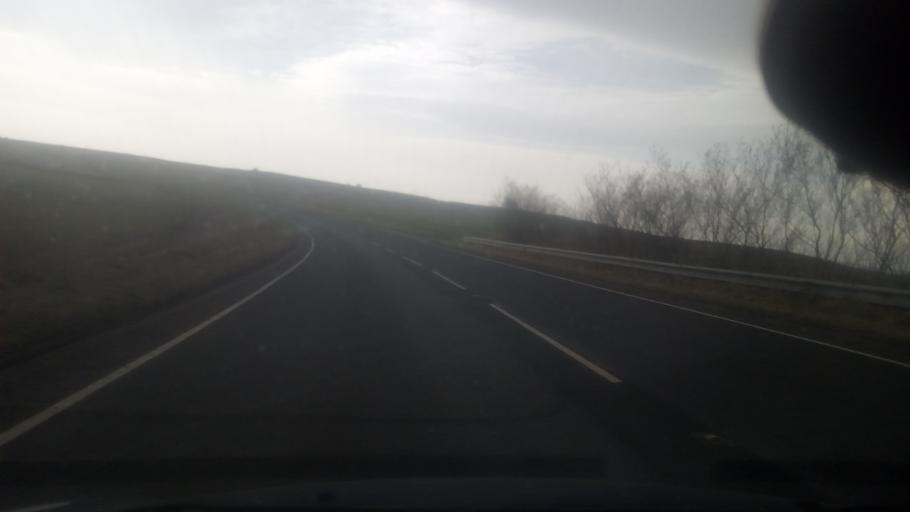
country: GB
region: England
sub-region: Northumberland
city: Corsenside
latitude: 55.1385
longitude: -2.1481
